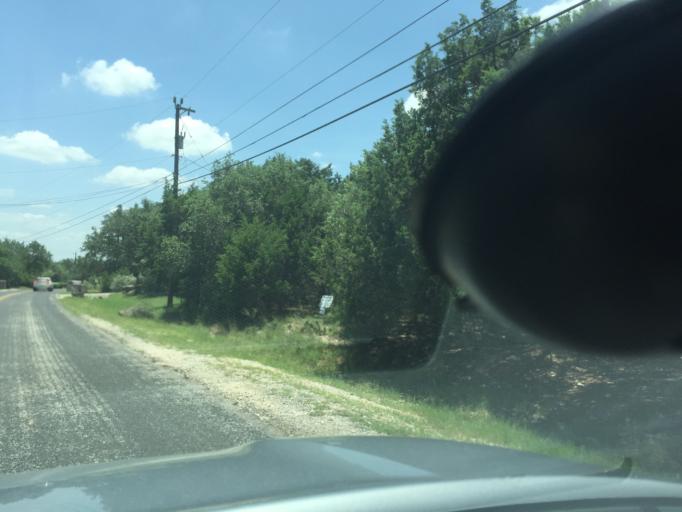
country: US
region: Texas
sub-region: Bexar County
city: Timberwood Park
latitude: 29.6978
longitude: -98.5065
